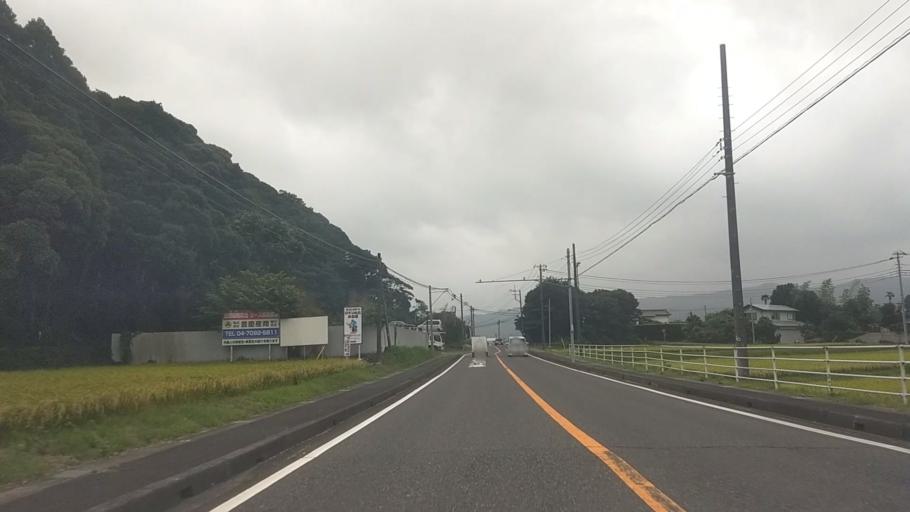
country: JP
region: Chiba
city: Kawaguchi
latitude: 35.1309
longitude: 140.0791
